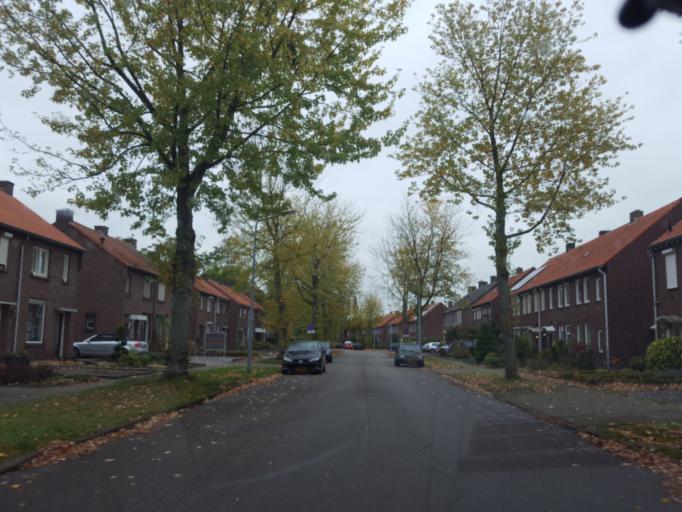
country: NL
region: Limburg
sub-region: Gemeente Weert
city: Weert
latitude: 51.2500
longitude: 5.7370
